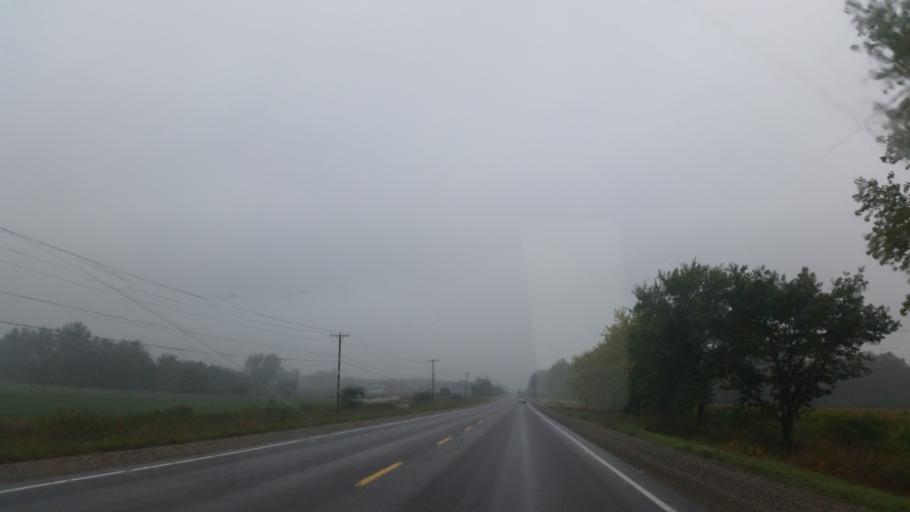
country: CA
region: Ontario
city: Stratford
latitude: 43.2791
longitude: -81.0605
